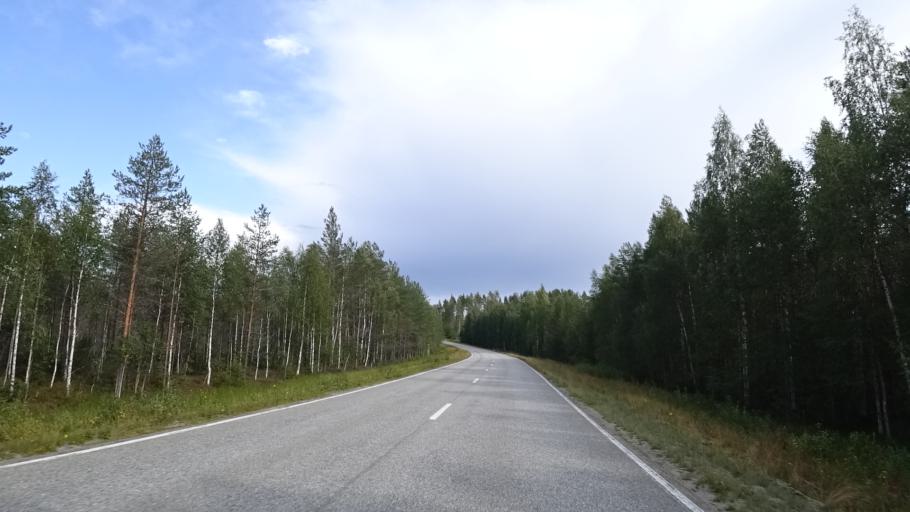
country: FI
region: North Karelia
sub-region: Joensuu
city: Ilomantsi
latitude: 62.6215
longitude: 31.1648
